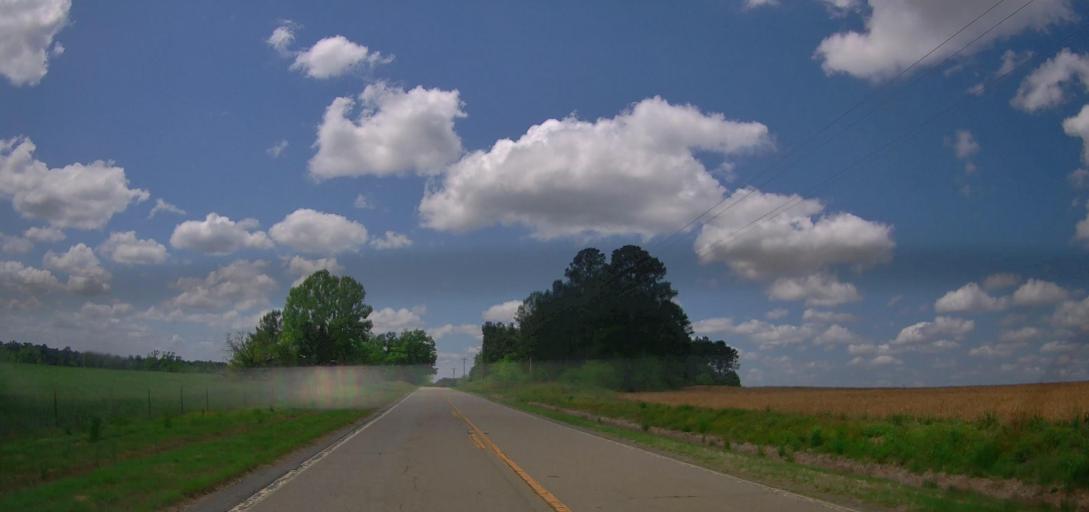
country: US
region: Georgia
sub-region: Dodge County
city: Chester
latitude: 32.5170
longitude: -83.2205
